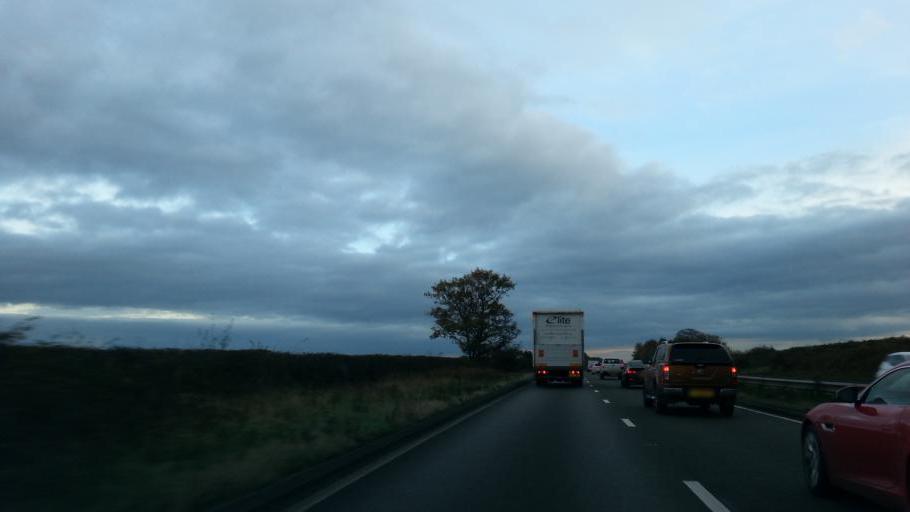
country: GB
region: England
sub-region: Nottinghamshire
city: Bircotes
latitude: 53.3574
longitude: -1.0427
